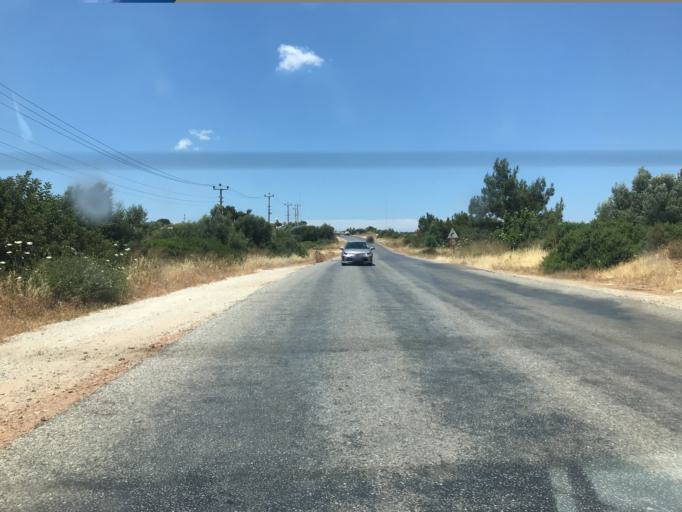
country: TR
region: Aydin
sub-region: Didim
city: Didim
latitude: 37.4128
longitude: 27.3783
